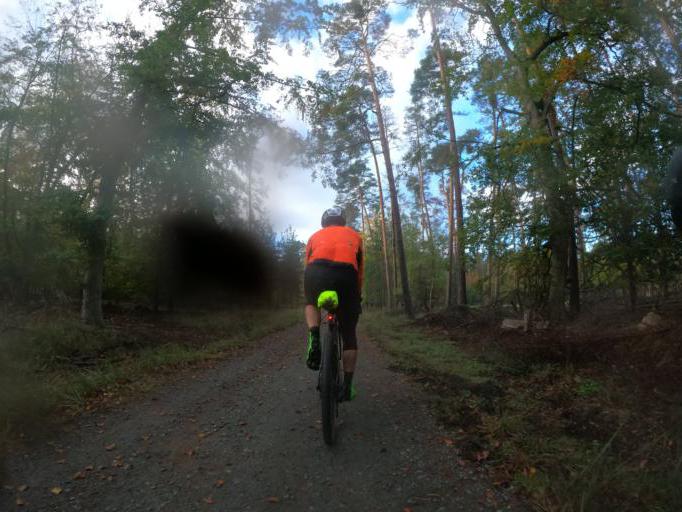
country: DE
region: Hesse
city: Raunheim
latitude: 49.9922
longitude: 8.4874
